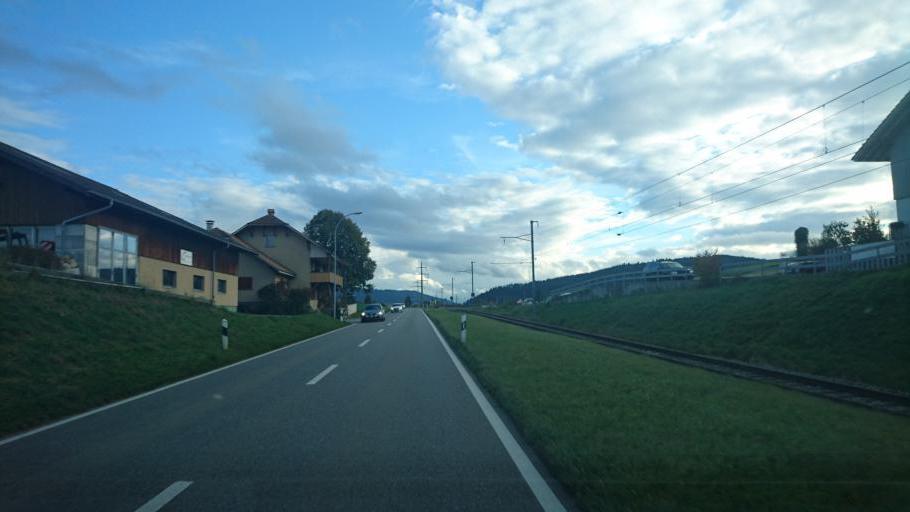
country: CH
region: Bern
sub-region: Bern-Mittelland District
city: Biglen
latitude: 46.9173
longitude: 7.6320
